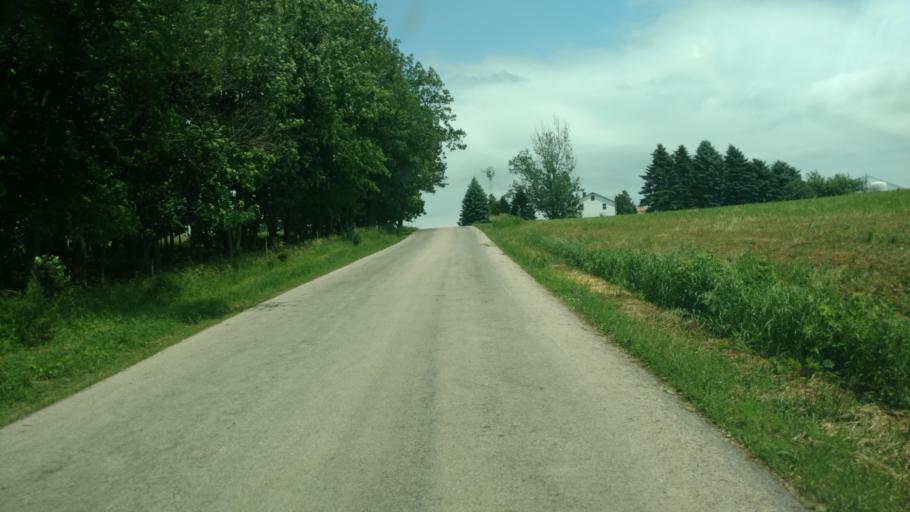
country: US
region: Wisconsin
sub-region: Monroe County
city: Cashton
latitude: 43.6874
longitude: -90.6748
